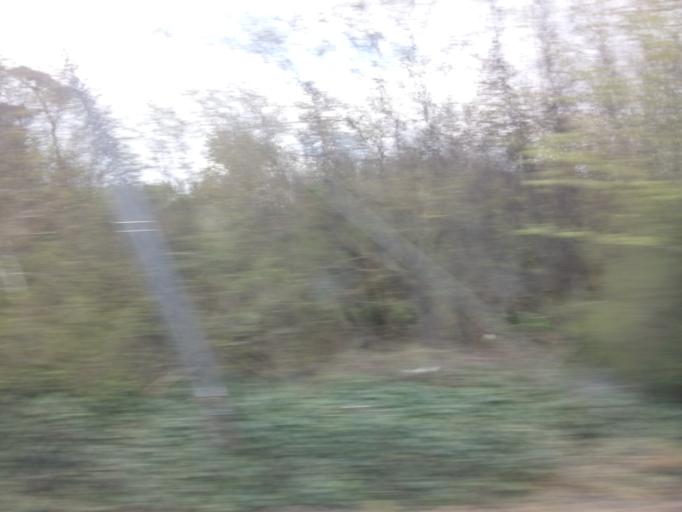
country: GB
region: Scotland
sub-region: East Lothian
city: Dunbar
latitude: 55.9835
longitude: -2.4901
